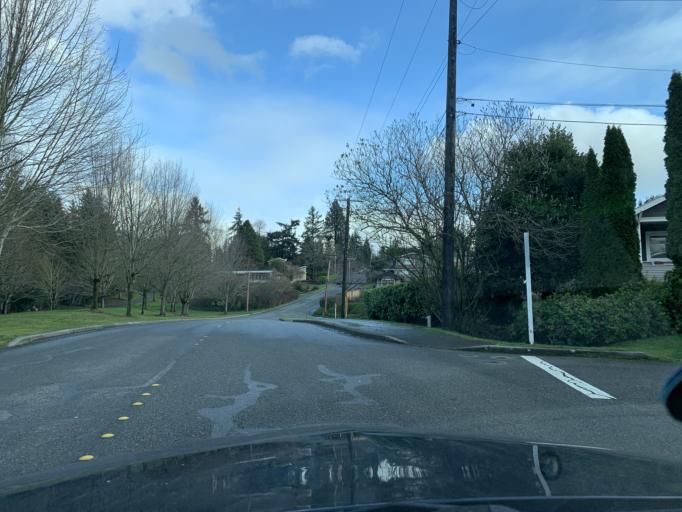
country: US
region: Washington
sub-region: King County
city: Mercer Island
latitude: 47.5890
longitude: -122.2511
